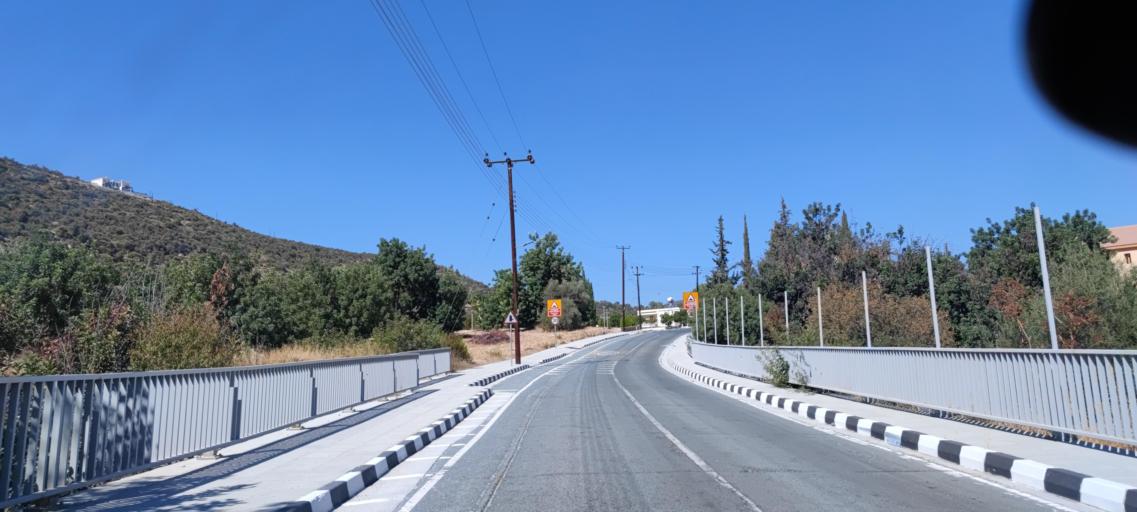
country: CY
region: Limassol
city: Mouttagiaka
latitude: 34.7737
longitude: 33.0489
